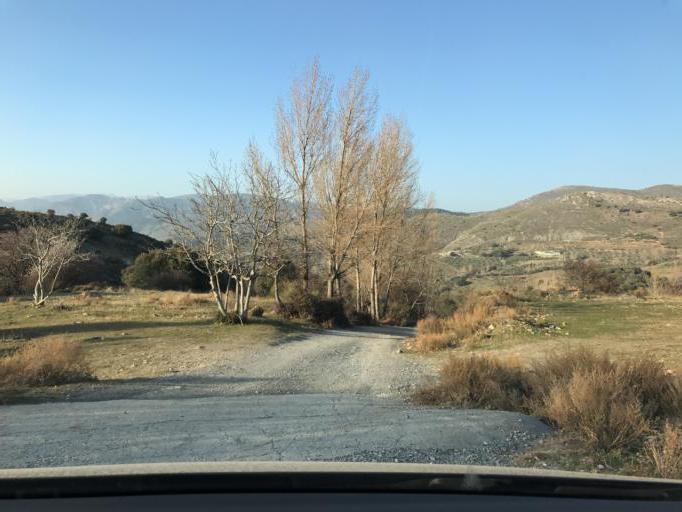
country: ES
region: Andalusia
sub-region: Provincia de Granada
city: Guejar-Sierra
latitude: 37.1798
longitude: -3.4297
